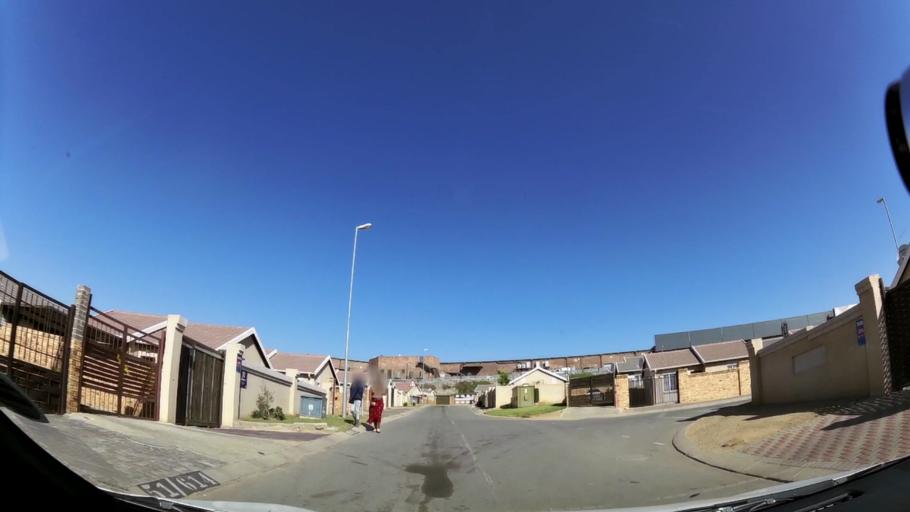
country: ZA
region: Gauteng
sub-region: West Rand District Municipality
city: Muldersdriseloop
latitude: -26.0117
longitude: 27.9401
